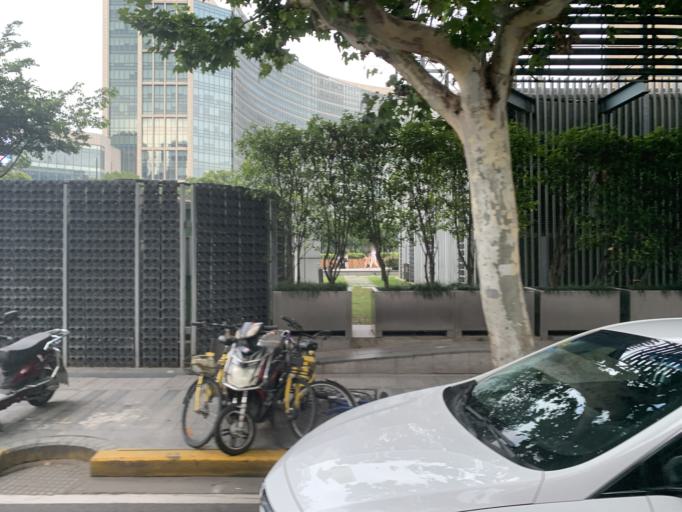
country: CN
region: Shanghai Shi
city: Pudong
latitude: 31.2309
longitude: 121.5212
